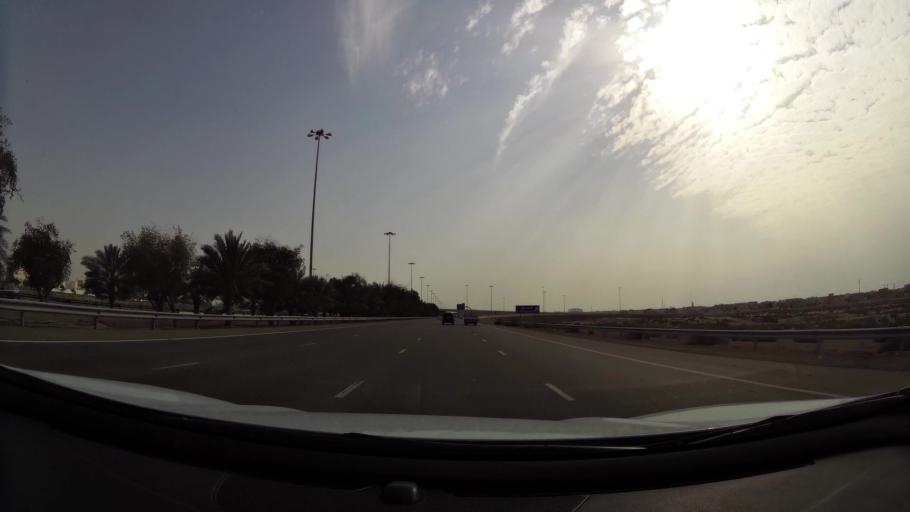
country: AE
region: Abu Dhabi
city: Abu Dhabi
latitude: 24.3735
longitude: 54.6562
